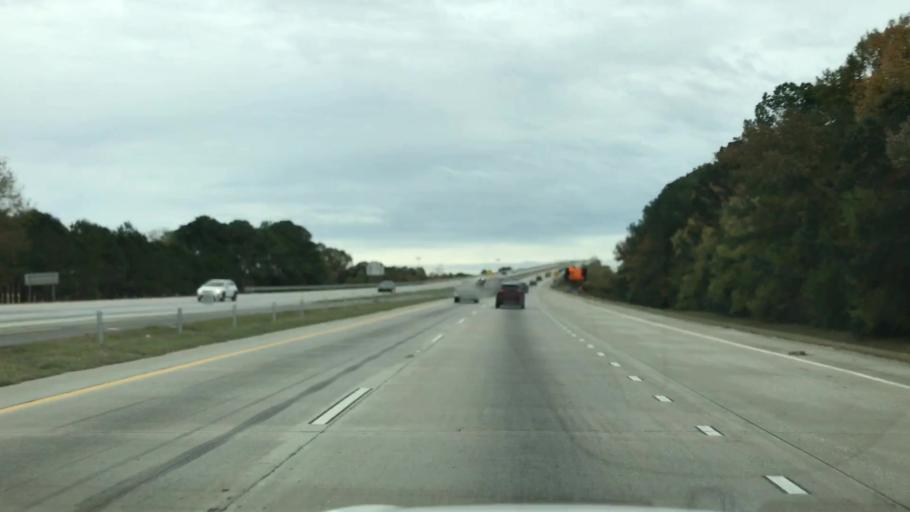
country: US
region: South Carolina
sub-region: Charleston County
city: North Charleston
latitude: 32.8669
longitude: -79.9078
